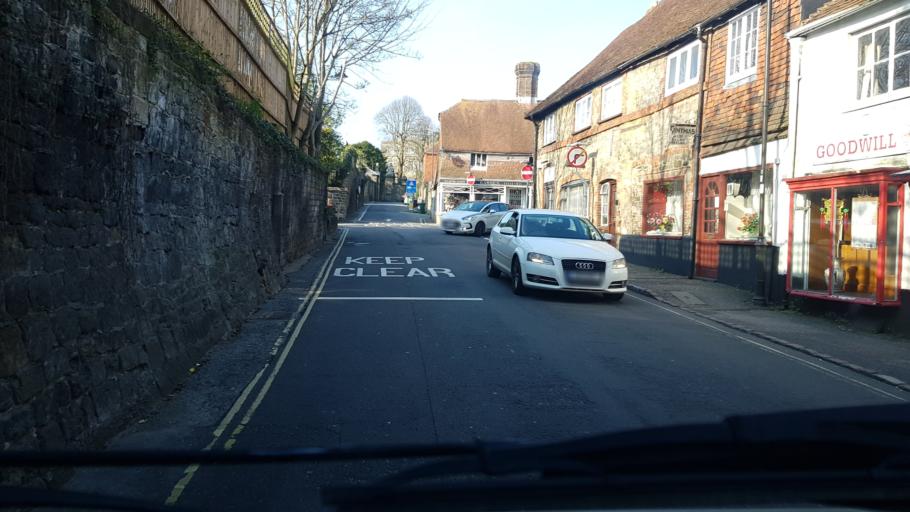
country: GB
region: England
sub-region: West Sussex
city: Petworth
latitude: 50.9857
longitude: -0.6111
